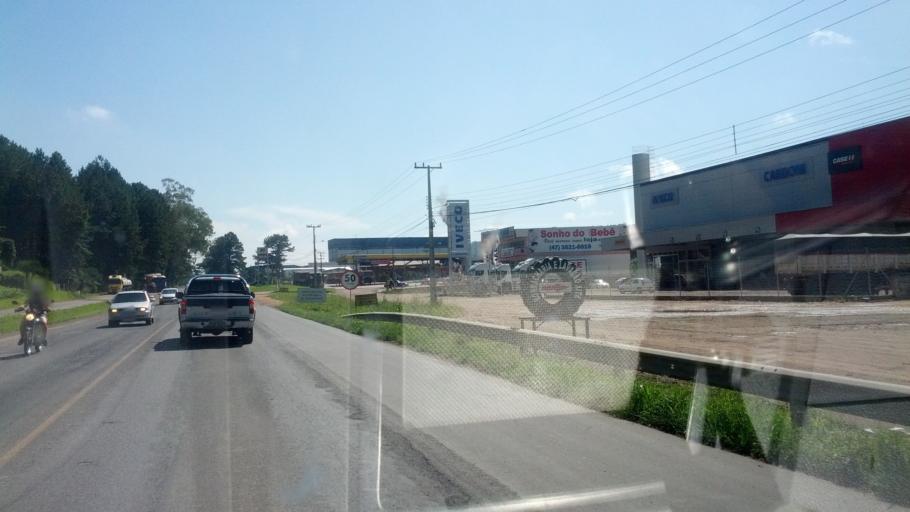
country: BR
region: Santa Catarina
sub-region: Rio Do Sul
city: Rio do Sul
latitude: -27.2435
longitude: -49.6901
